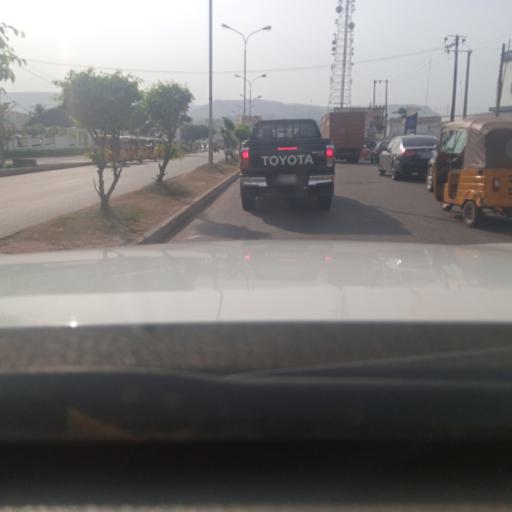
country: NG
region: Enugu
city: Enugu
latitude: 6.4412
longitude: 7.5102
